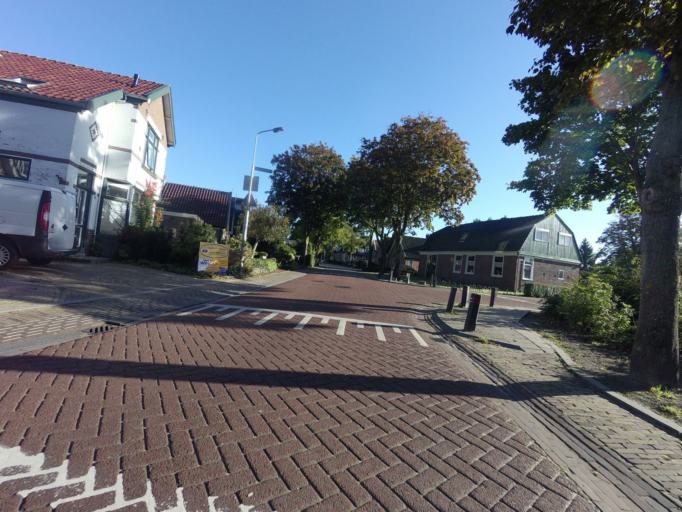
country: NL
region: North Holland
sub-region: Gemeente Langedijk
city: Broek op Langedijk
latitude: 52.6628
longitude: 4.7847
